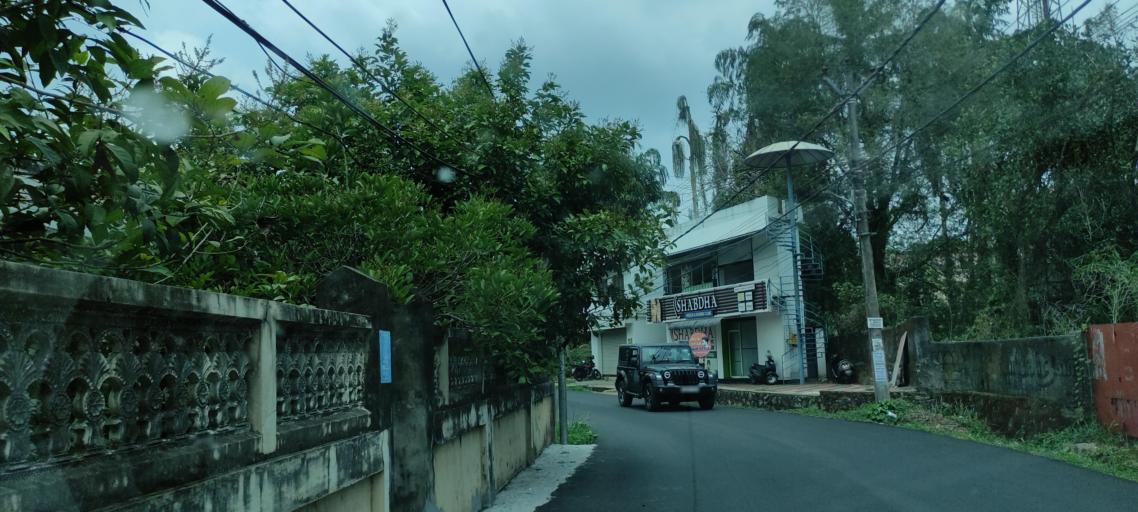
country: IN
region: Kerala
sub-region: Pattanamtitta
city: Adur
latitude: 9.1552
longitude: 76.7295
